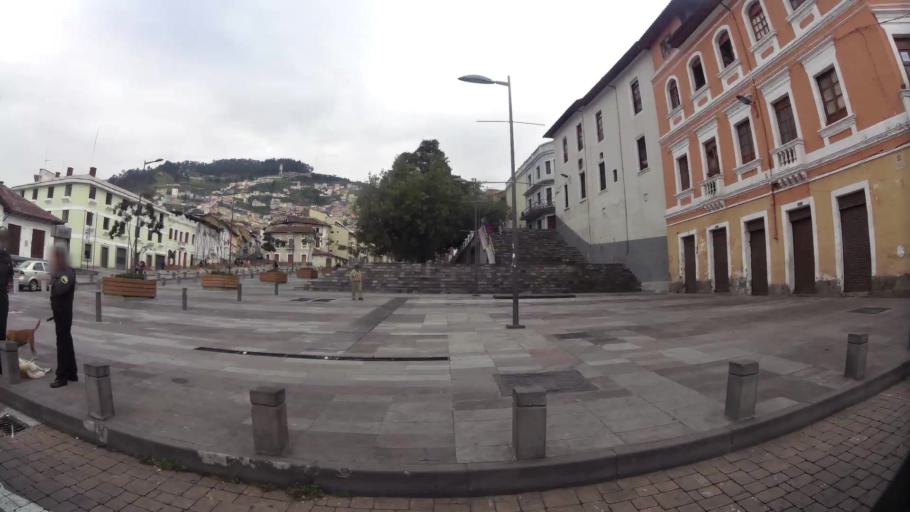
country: EC
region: Pichincha
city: Quito
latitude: -0.2230
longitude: -78.5165
